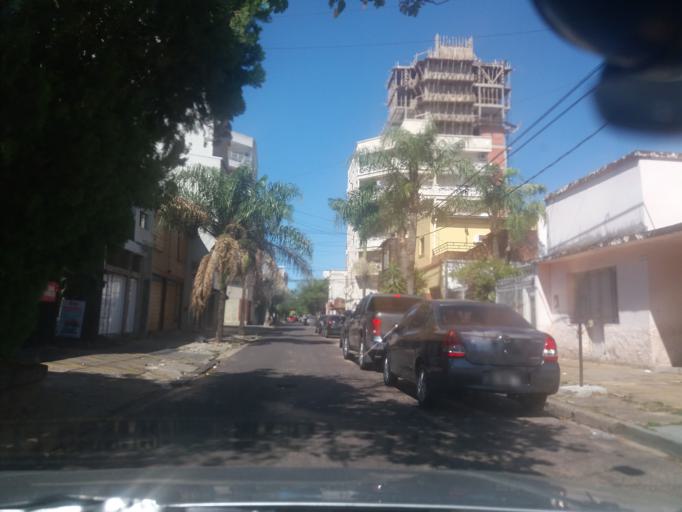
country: AR
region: Corrientes
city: Corrientes
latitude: -27.4686
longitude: -58.8469
